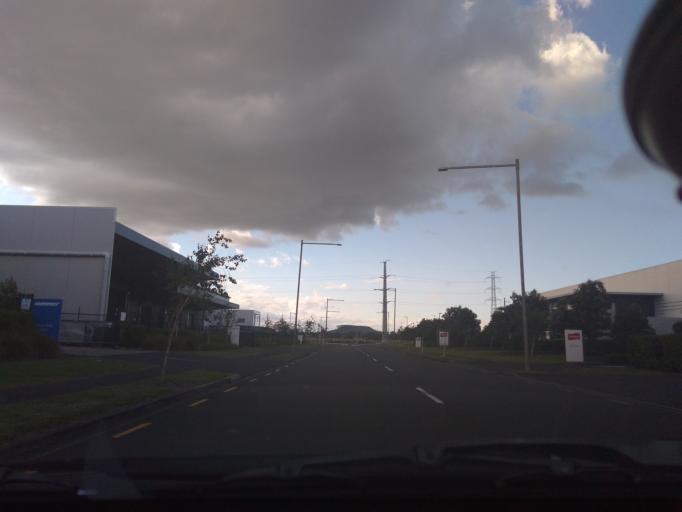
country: NZ
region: Auckland
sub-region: Auckland
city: Tamaki
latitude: -36.9313
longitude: 174.8751
